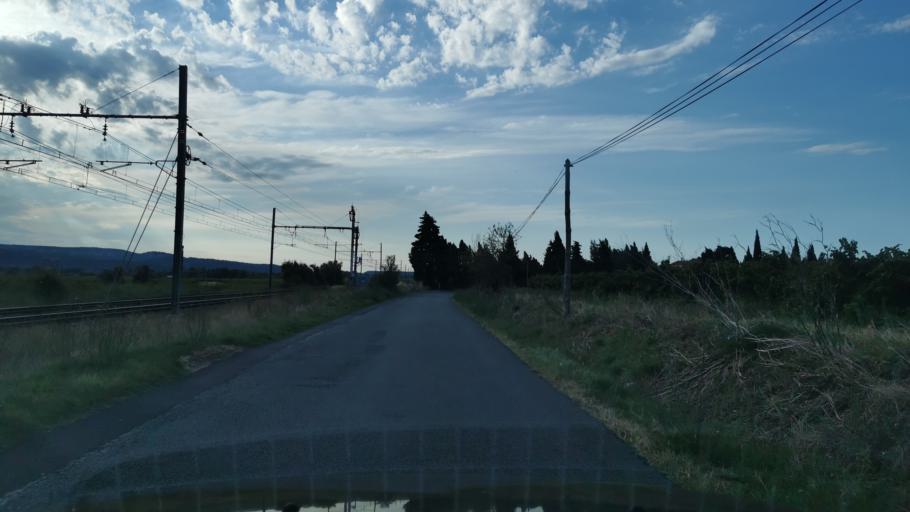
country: FR
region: Languedoc-Roussillon
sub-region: Departement de l'Aude
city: Narbonne
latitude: 43.1552
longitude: 3.0147
